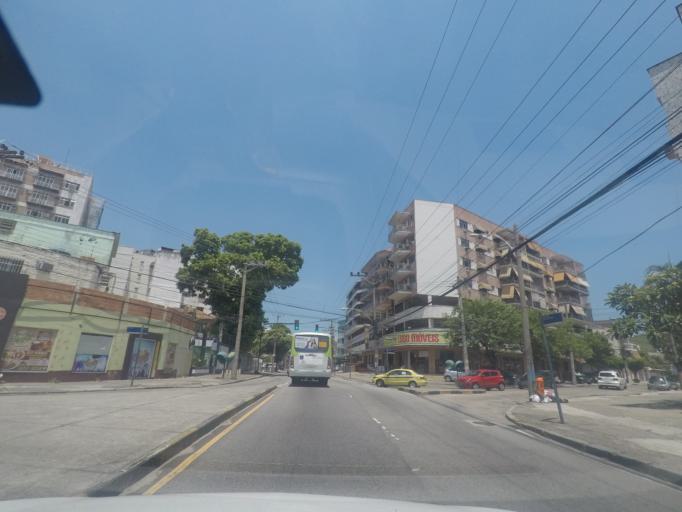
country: BR
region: Rio de Janeiro
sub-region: Duque De Caxias
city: Duque de Caxias
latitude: -22.8407
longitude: -43.3044
